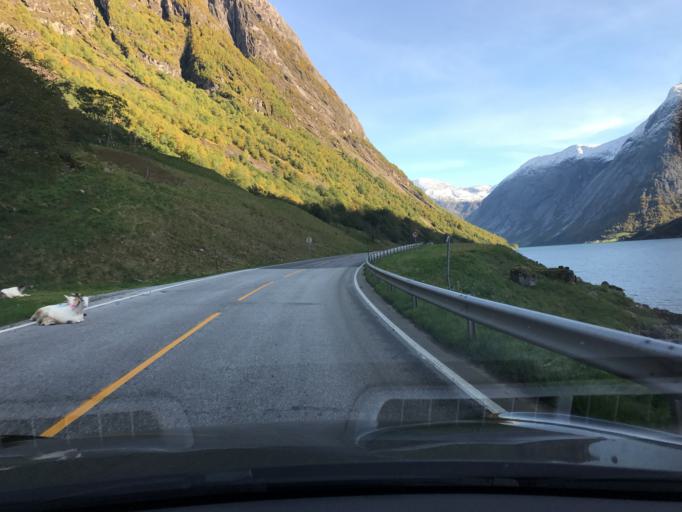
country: NO
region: Sogn og Fjordane
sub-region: Jolster
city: Skei
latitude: 61.5433
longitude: 6.5258
